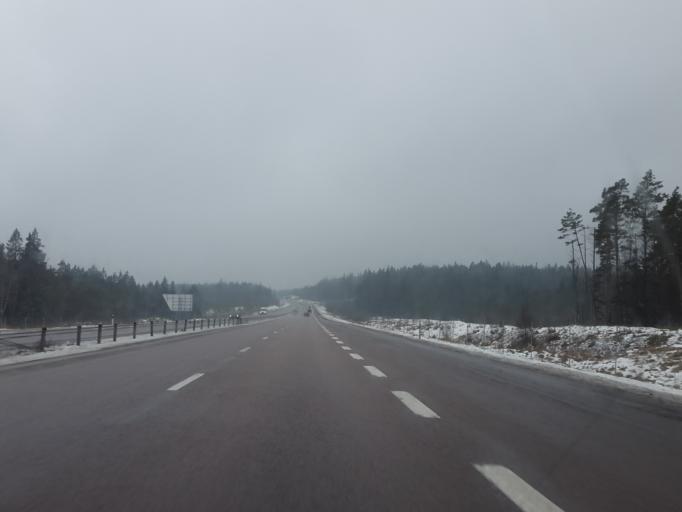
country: SE
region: Vaestra Goetaland
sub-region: Boras Kommun
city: Dalsjofors
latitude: 57.7566
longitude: 13.0959
